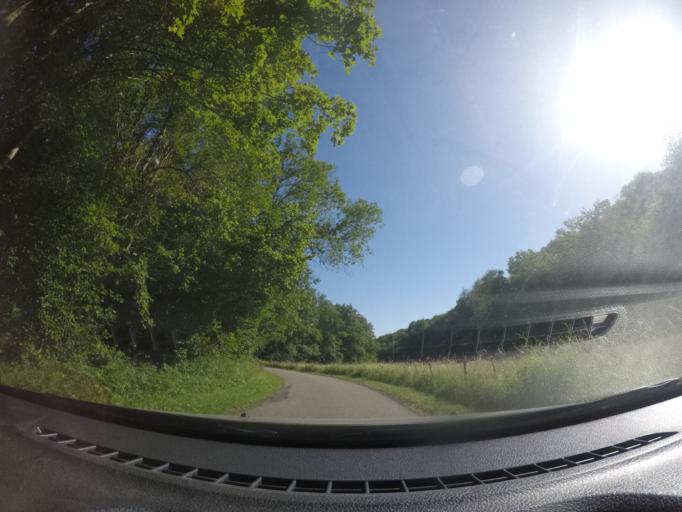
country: BE
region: Wallonia
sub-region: Province de Namur
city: Philippeville
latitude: 50.1728
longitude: 4.5577
